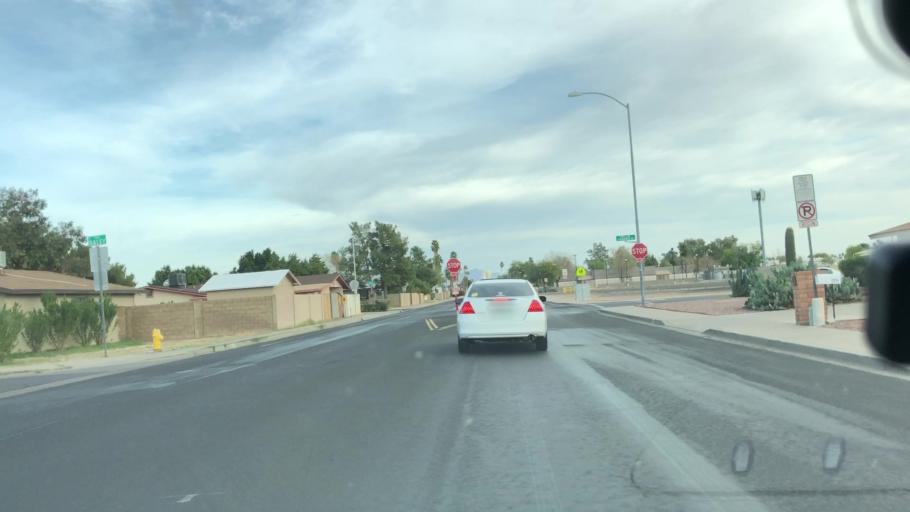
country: US
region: Arizona
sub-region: Maricopa County
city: Mesa
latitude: 33.4007
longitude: -111.7974
